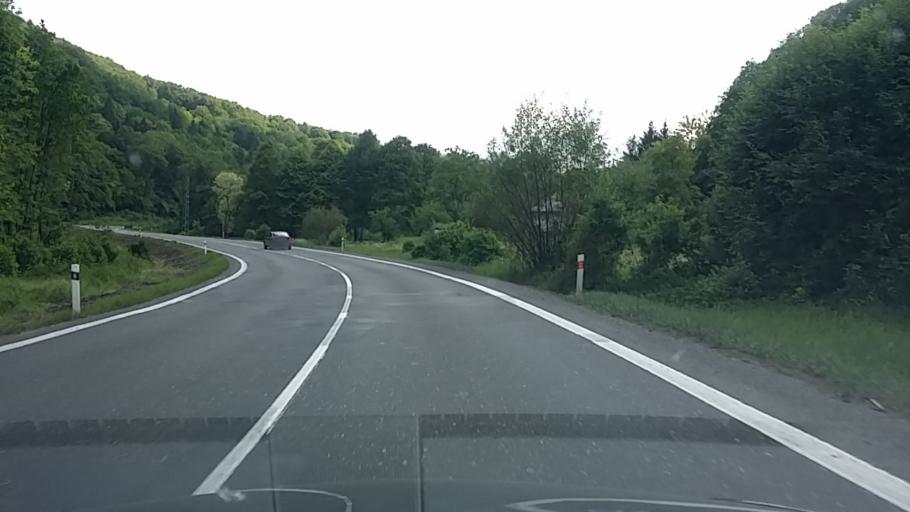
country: SK
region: Banskobystricky
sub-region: Okres Banska Bystrica
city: Zvolen
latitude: 48.5406
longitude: 19.1216
